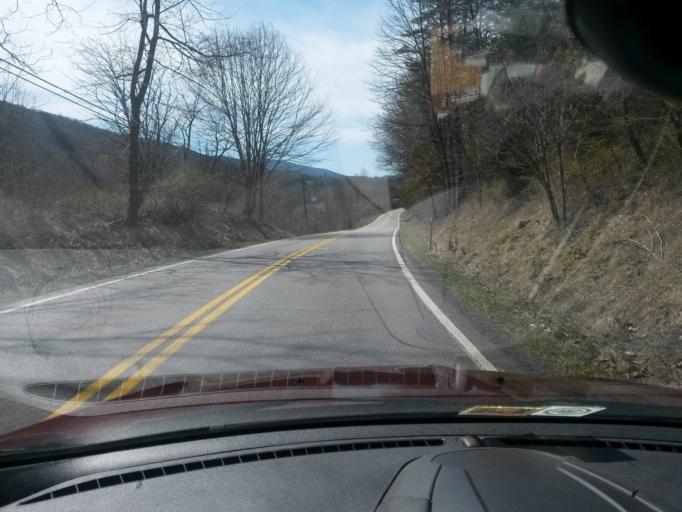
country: US
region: Virginia
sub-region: City of Covington
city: Covington
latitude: 37.7991
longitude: -80.0760
